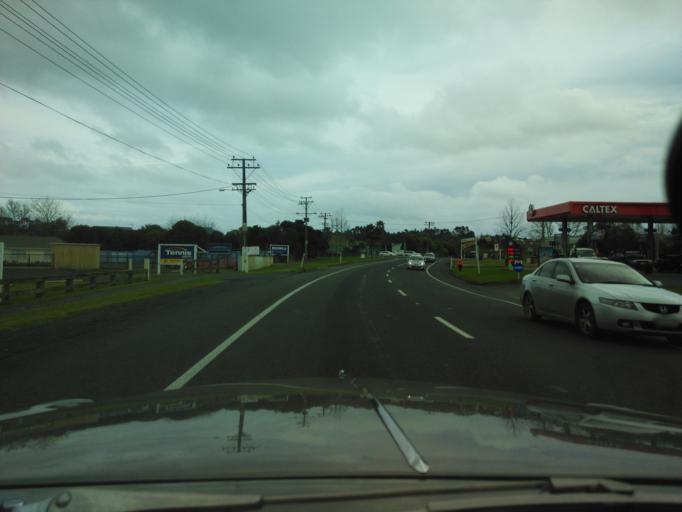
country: NZ
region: Auckland
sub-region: Auckland
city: Muriwai Beach
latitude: -36.7687
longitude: 174.4936
